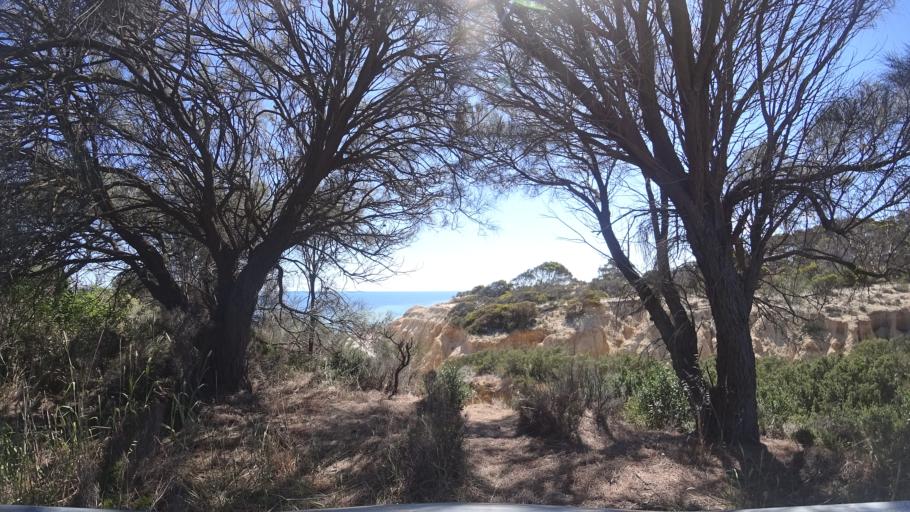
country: AU
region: South Australia
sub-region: Kangaroo Island
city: Kingscote
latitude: -35.7366
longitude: 137.7185
